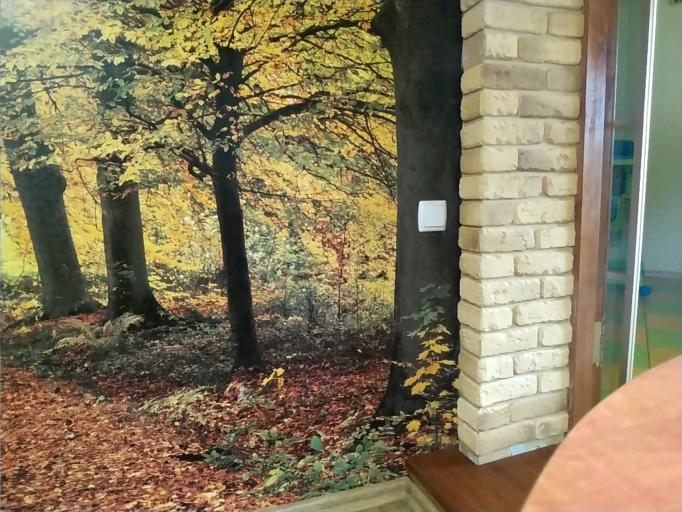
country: RU
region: Smolensk
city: Dorogobuzh
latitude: 54.8888
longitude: 33.3081
